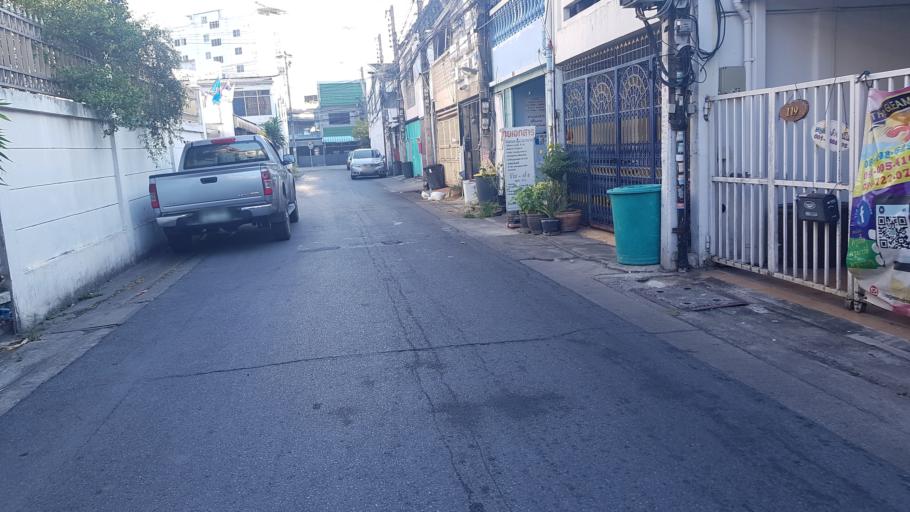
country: TH
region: Bangkok
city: Wang Thonglang
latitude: 13.7796
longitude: 100.6253
